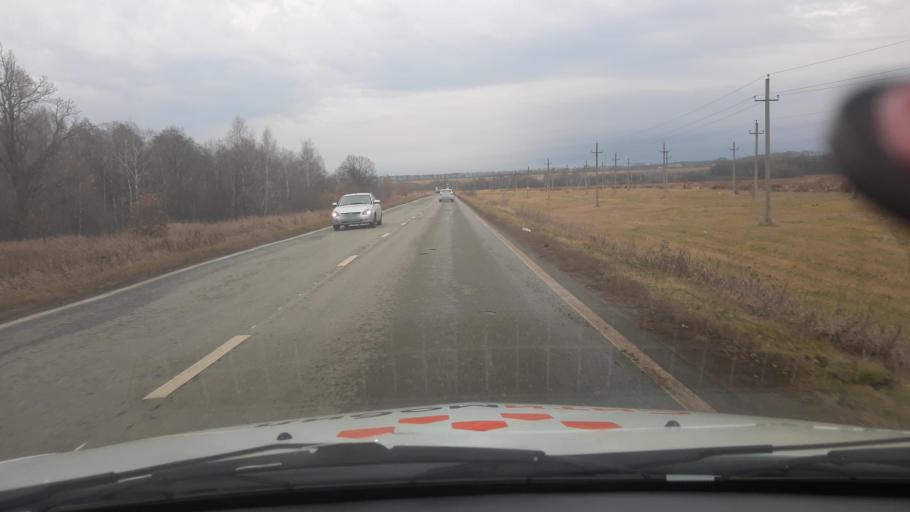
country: RU
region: Bashkortostan
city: Iglino
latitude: 54.7427
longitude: 56.2203
